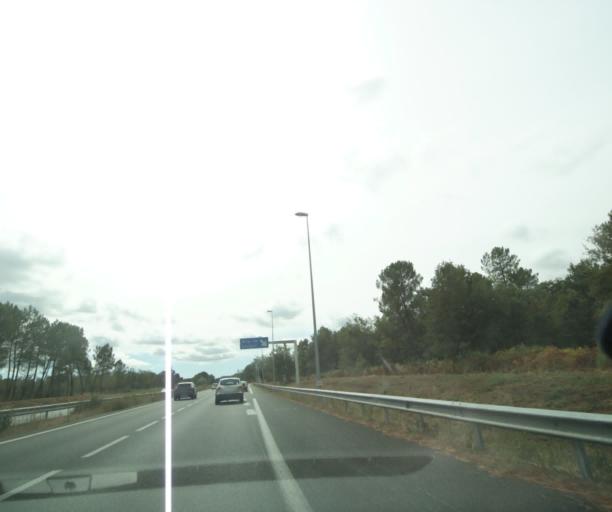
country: FR
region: Aquitaine
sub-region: Departement de la Gironde
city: Reignac
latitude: 45.1936
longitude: -0.4937
